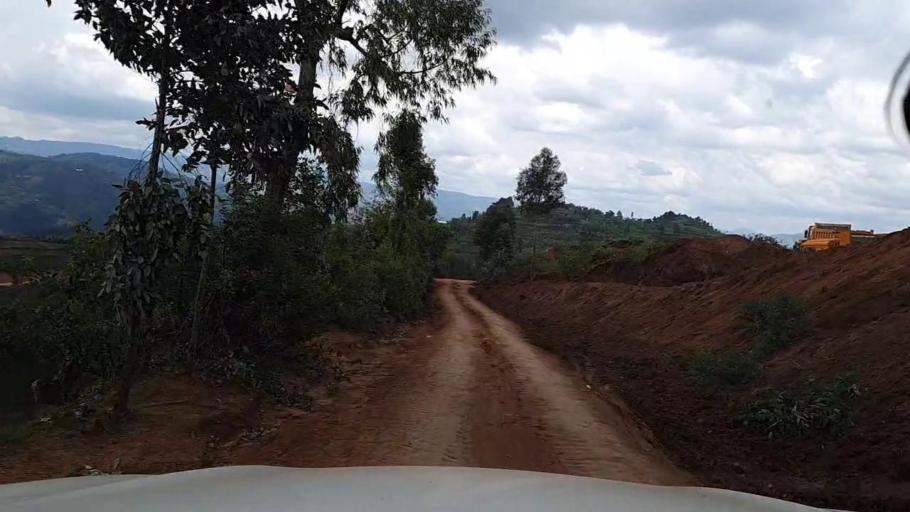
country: RW
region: Southern Province
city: Nzega
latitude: -2.7065
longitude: 29.5100
